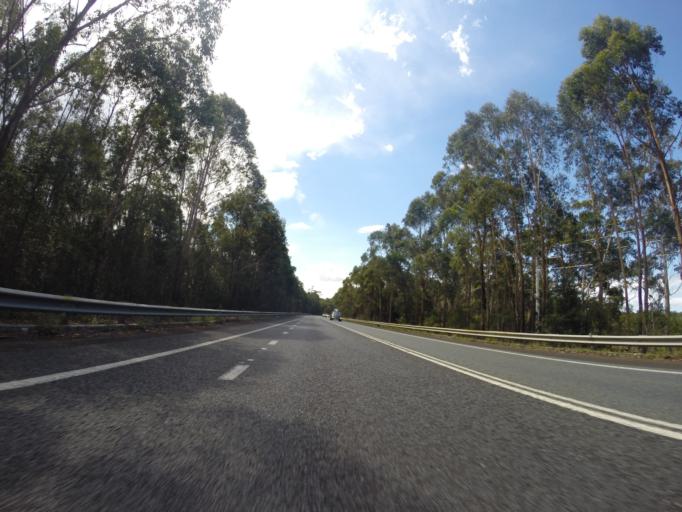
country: AU
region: New South Wales
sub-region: Shoalhaven Shire
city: Falls Creek
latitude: -35.0339
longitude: 150.5830
